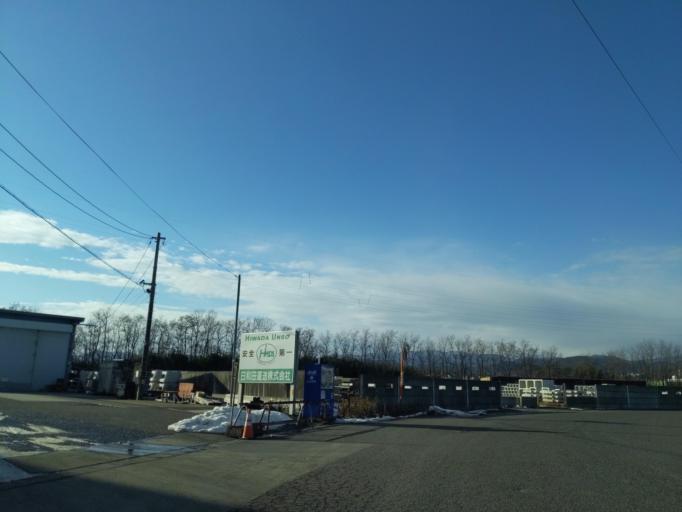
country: JP
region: Fukushima
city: Motomiya
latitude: 37.4713
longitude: 140.3735
